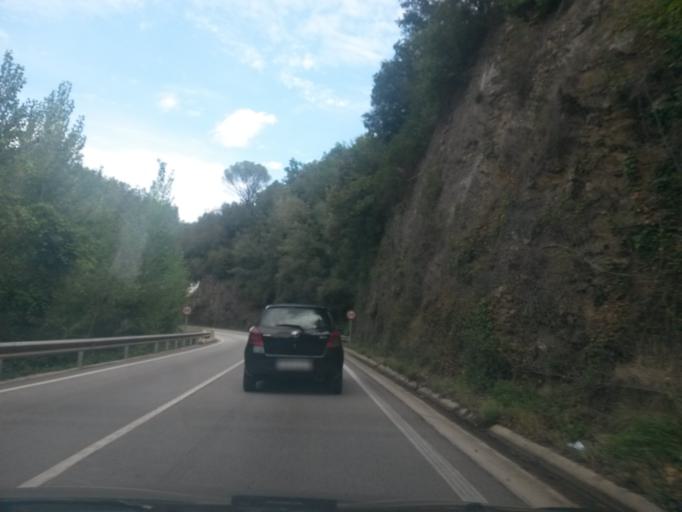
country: ES
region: Catalonia
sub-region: Provincia de Girona
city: Angles
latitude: 41.9651
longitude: 2.6742
